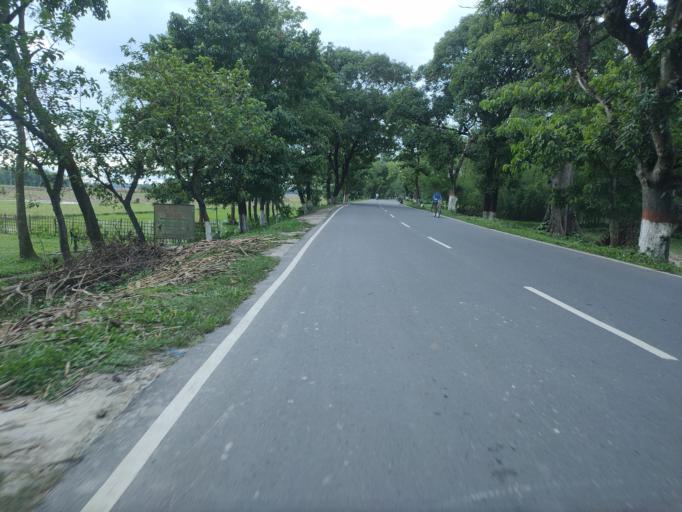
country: IN
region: West Bengal
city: Kishanganj
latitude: 26.1725
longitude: 87.9118
